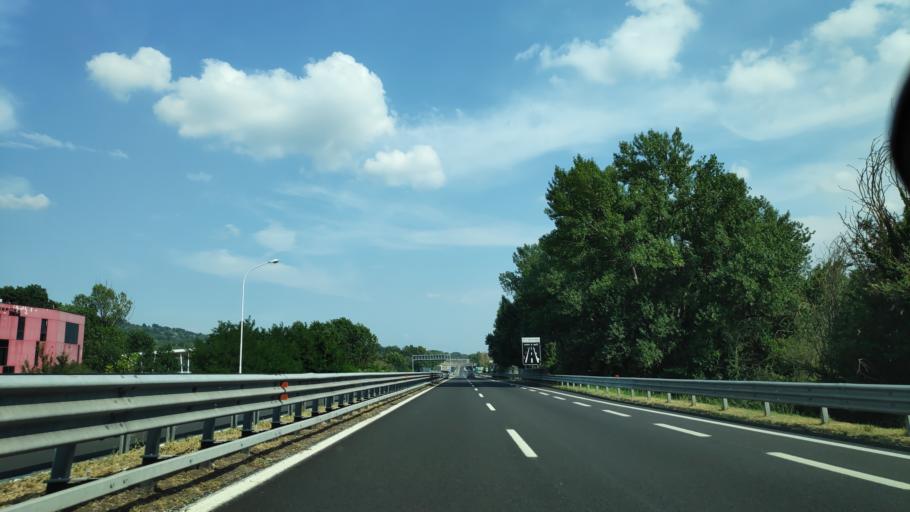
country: IT
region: Umbria
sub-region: Provincia di Terni
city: Attigliano
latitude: 42.5076
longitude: 12.2968
